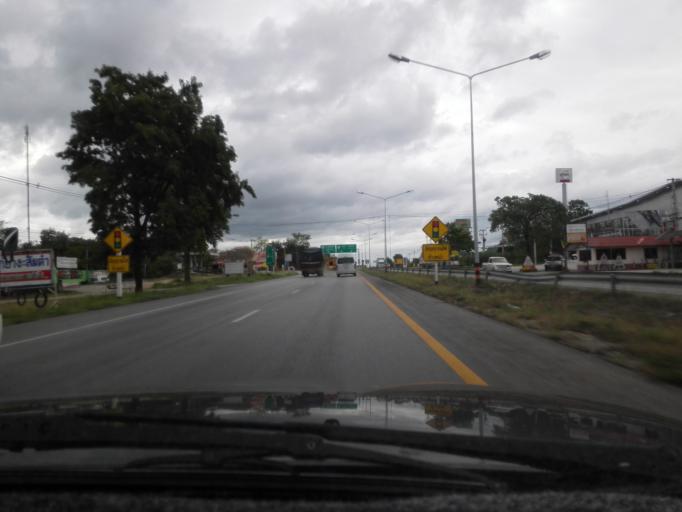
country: TH
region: Tak
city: Tak
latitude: 16.8385
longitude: 99.1155
